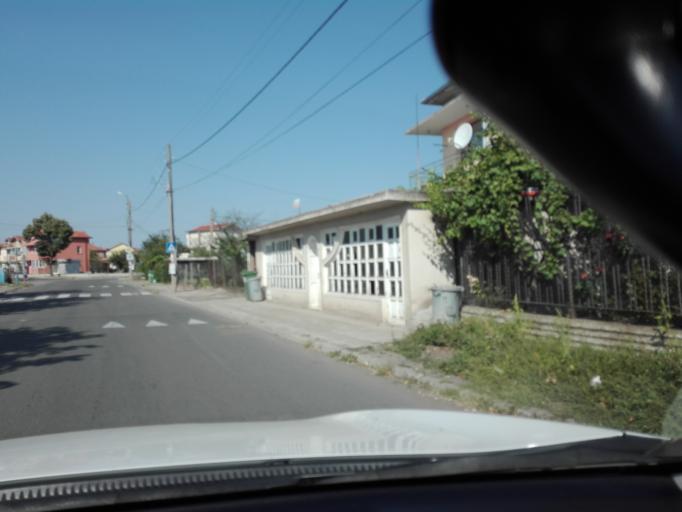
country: BG
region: Burgas
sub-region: Obshtina Kameno
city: Kameno
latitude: 42.6274
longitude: 27.3917
